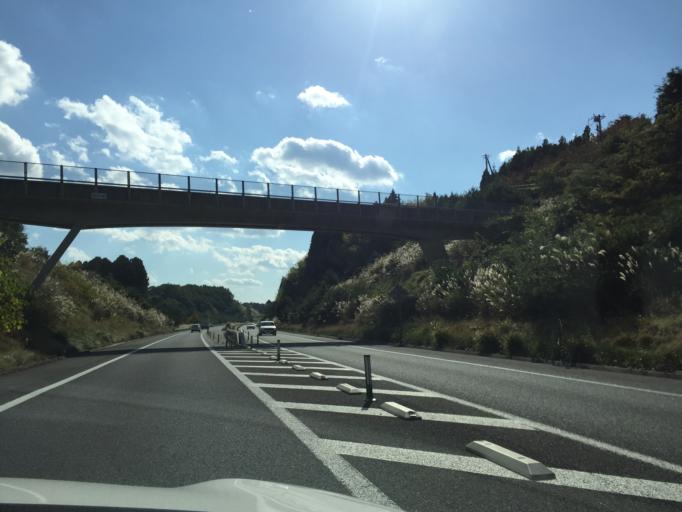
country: JP
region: Fukushima
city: Iwaki
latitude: 37.1975
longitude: 140.9865
